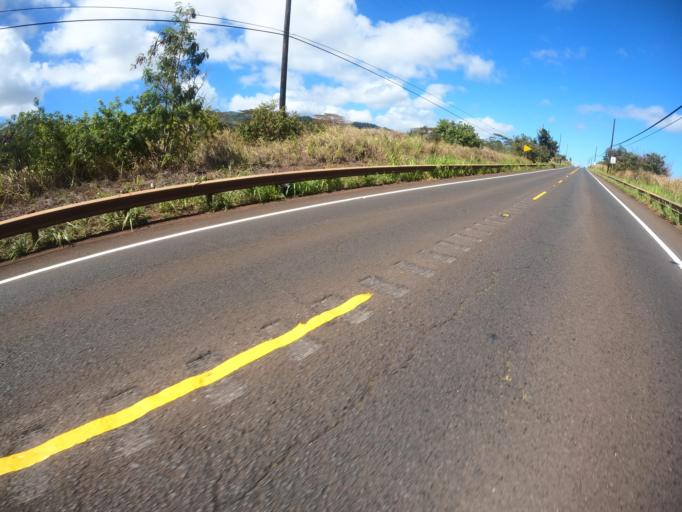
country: US
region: Hawaii
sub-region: Honolulu County
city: Waipi'o Acres
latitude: 21.4475
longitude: -158.0600
